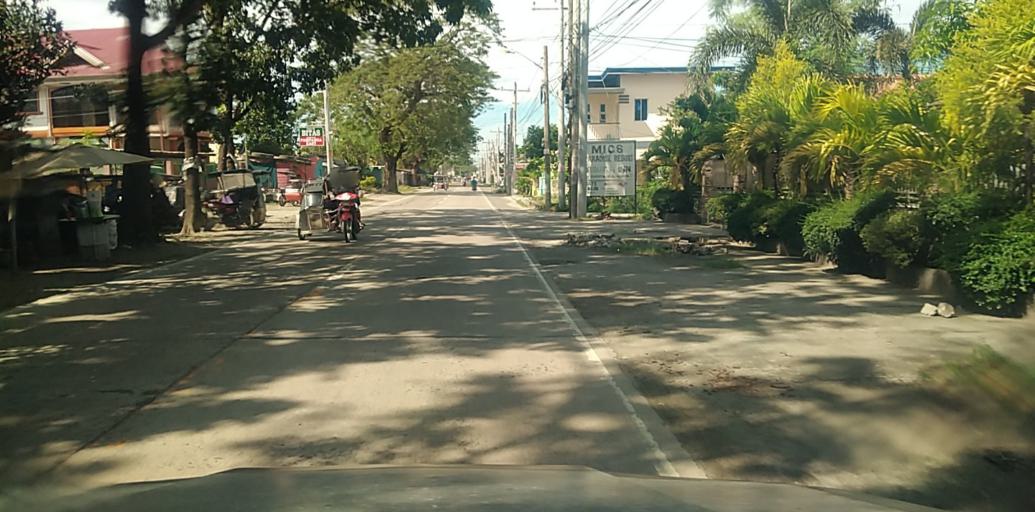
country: PH
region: Central Luzon
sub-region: Province of Pampanga
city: Anao
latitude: 15.1543
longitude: 120.7255
